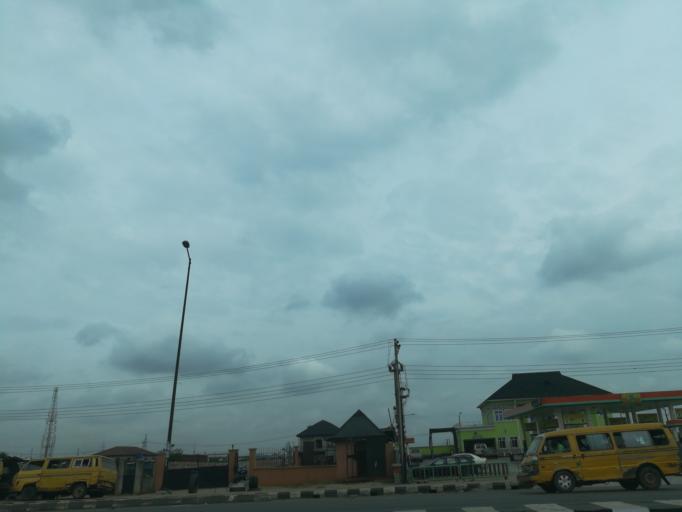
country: NG
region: Lagos
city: Ojota
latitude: 6.6047
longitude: 3.4060
